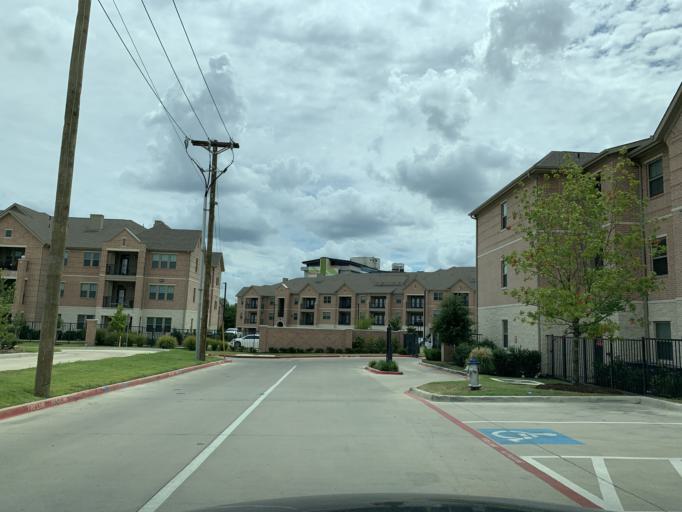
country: US
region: Texas
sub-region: Dallas County
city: Cockrell Hill
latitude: 32.7594
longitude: -96.8607
